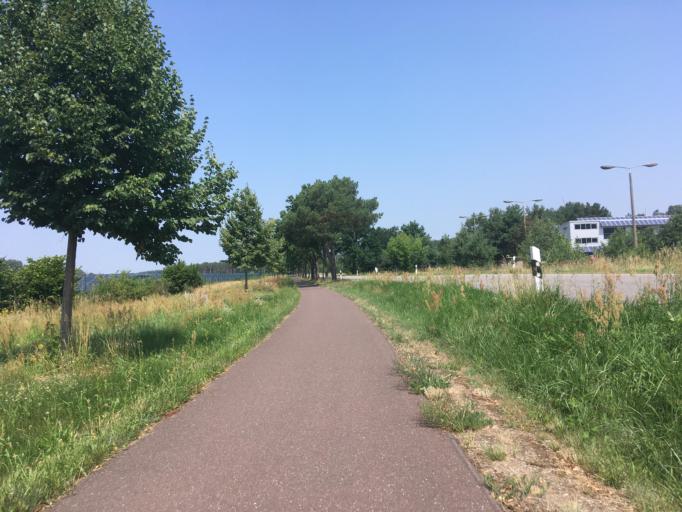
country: DE
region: Brandenburg
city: Brandenburg an der Havel
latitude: 52.3414
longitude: 12.5479
